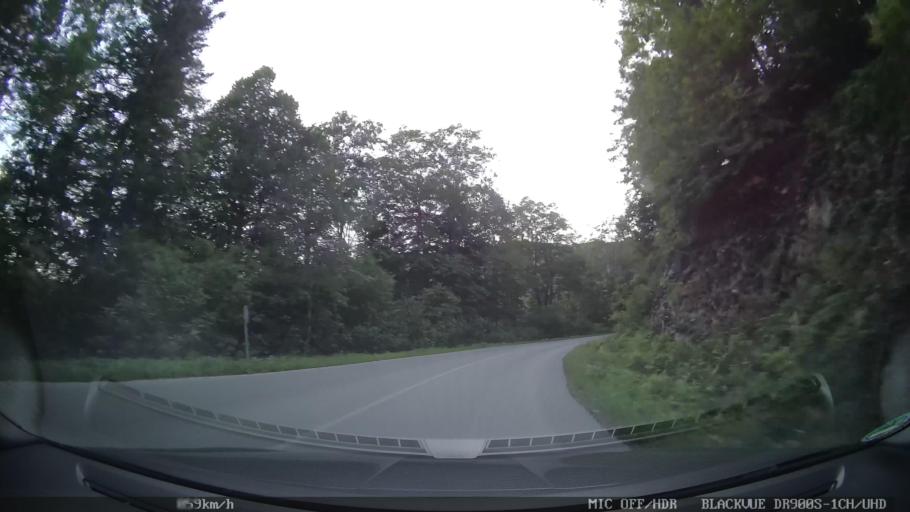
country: HR
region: Primorsko-Goranska
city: Vrbovsko
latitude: 45.1977
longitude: 15.0205
